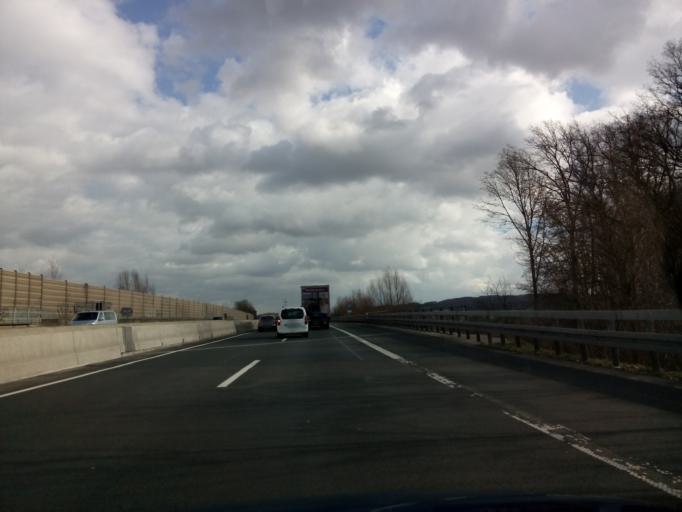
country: DE
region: Lower Saxony
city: Osnabrueck
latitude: 52.2433
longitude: 8.0993
